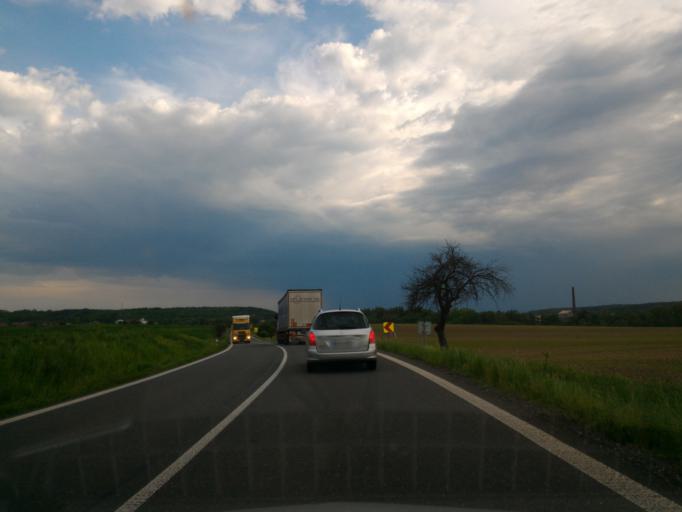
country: CZ
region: Central Bohemia
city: Lustenice
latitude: 50.2814
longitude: 14.9554
